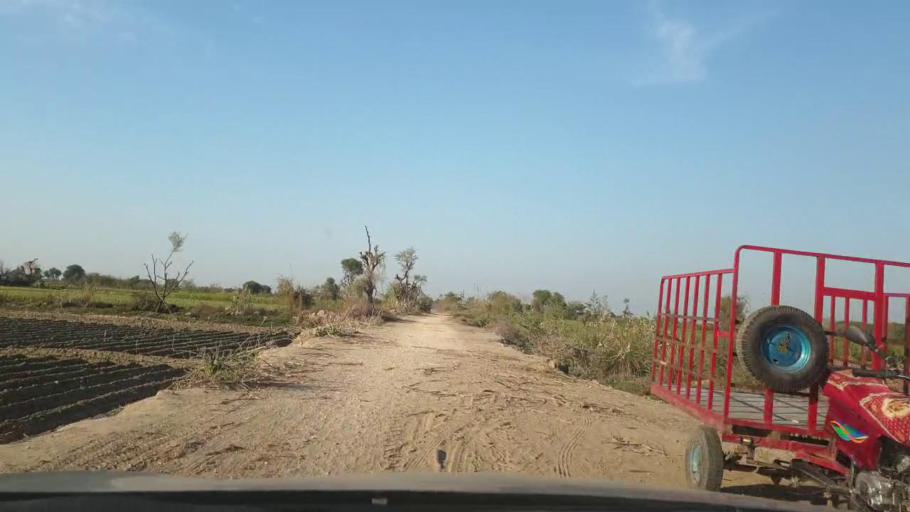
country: PK
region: Sindh
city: Tando Adam
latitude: 25.6976
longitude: 68.7023
